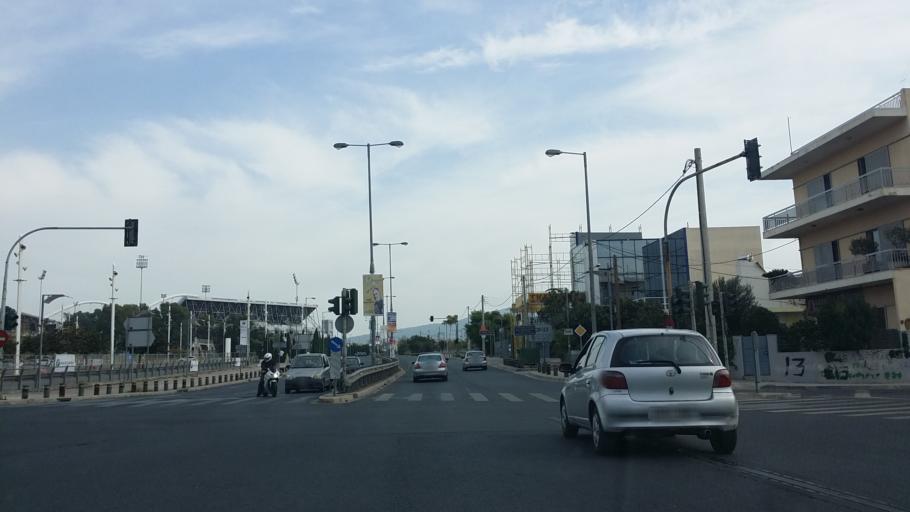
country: GR
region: Attica
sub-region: Nomarchia Athinas
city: Filothei
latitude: 38.0405
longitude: 23.7764
